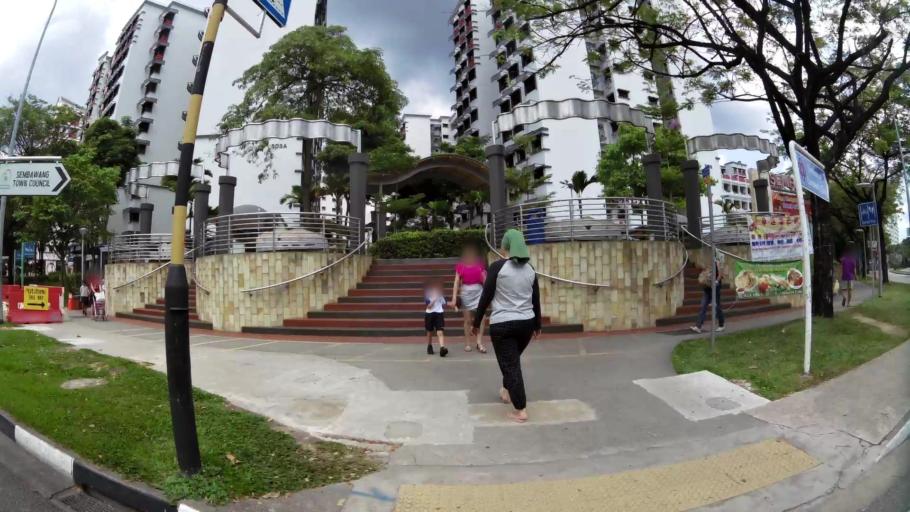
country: MY
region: Johor
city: Kampung Pasir Gudang Baru
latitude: 1.4500
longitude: 103.8216
